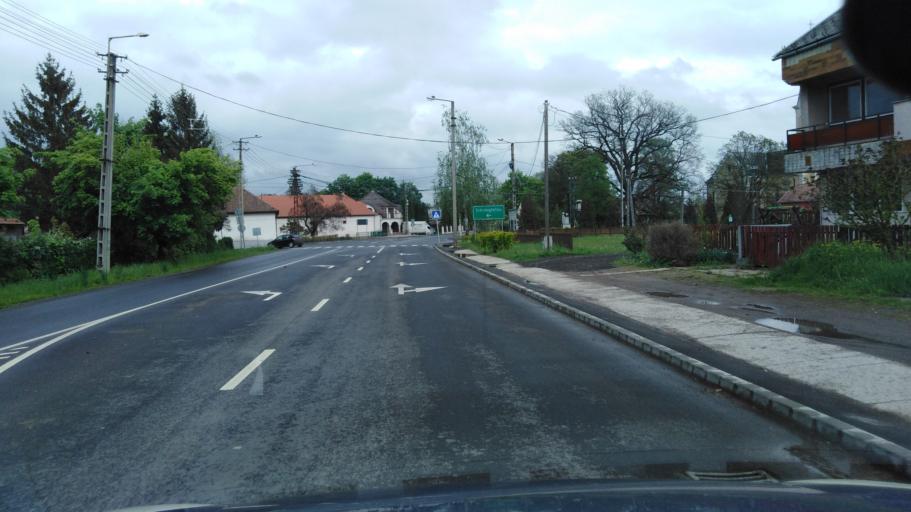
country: HU
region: Nograd
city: Szecseny
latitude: 48.1271
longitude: 19.5749
